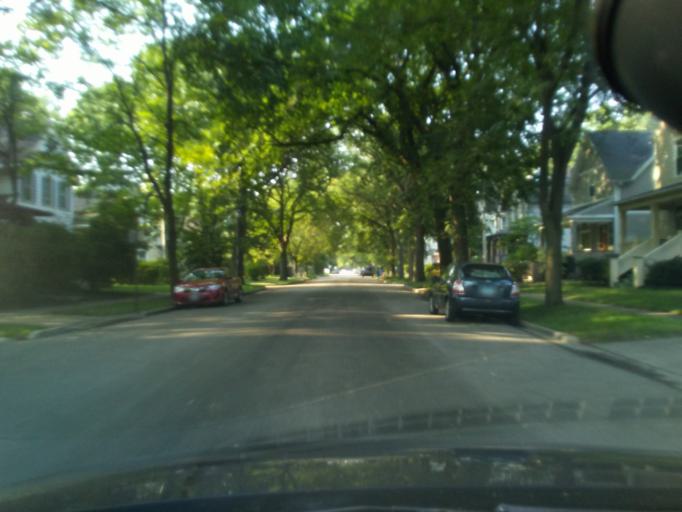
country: US
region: Illinois
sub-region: Cook County
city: Evanston
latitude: 42.0392
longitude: -87.6837
